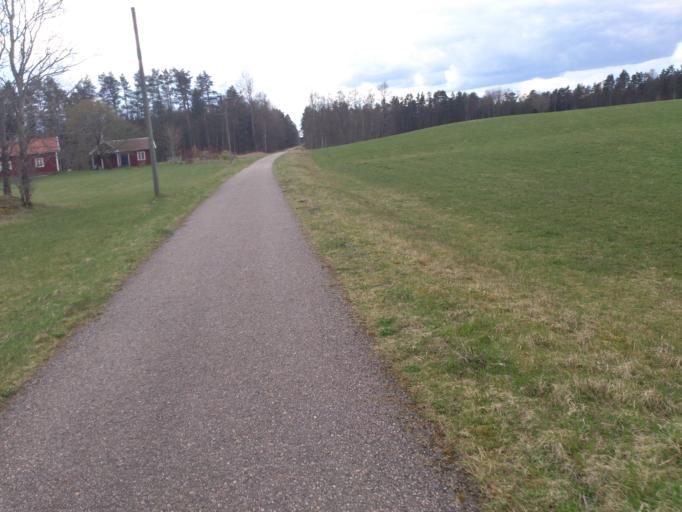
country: SE
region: Vaestra Goetaland
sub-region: Falkopings Kommun
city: Falkoeping
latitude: 57.9781
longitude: 13.5226
